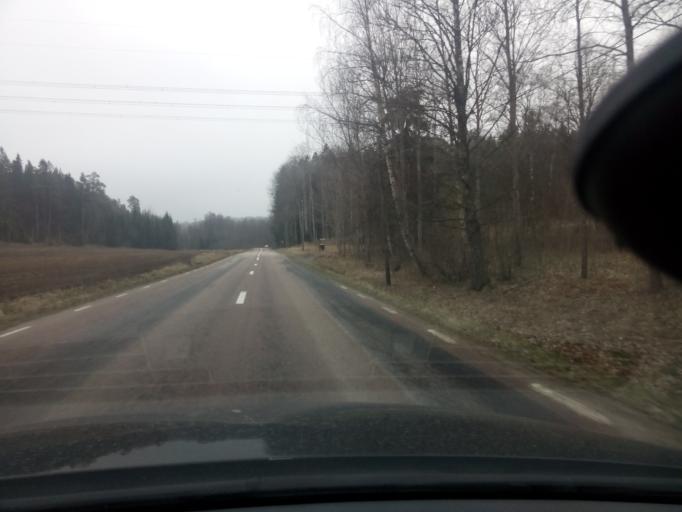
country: SE
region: Soedermanland
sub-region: Gnesta Kommun
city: Gnesta
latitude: 59.0049
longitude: 17.1752
